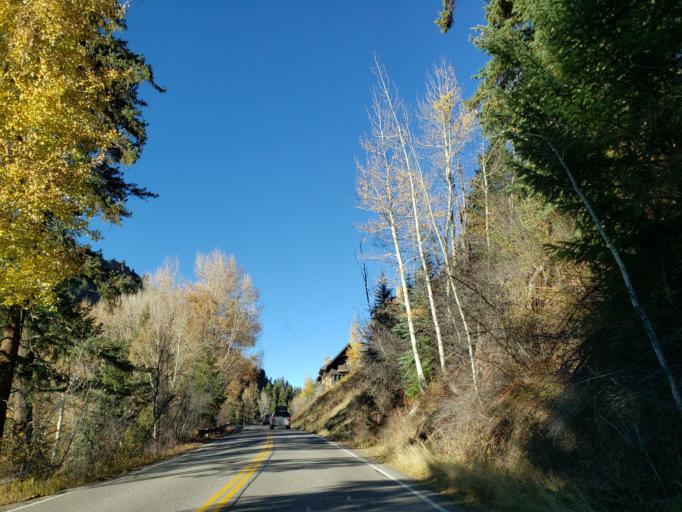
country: US
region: Colorado
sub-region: Pitkin County
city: Aspen
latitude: 39.1797
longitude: -106.8591
